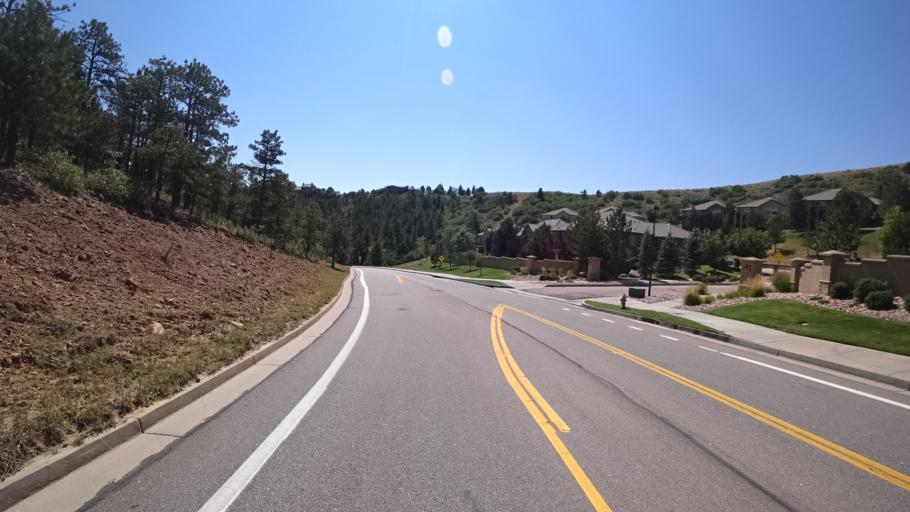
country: US
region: Colorado
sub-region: El Paso County
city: Air Force Academy
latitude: 38.9404
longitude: -104.8715
